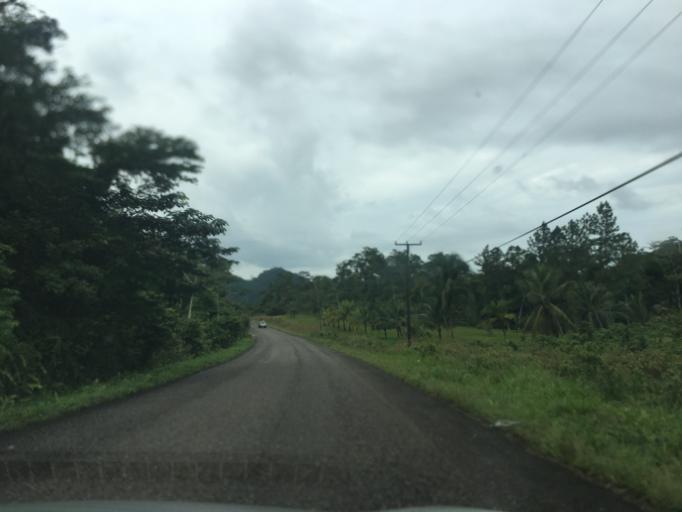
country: BZ
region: Cayo
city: Belmopan
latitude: 17.0866
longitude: -88.6038
